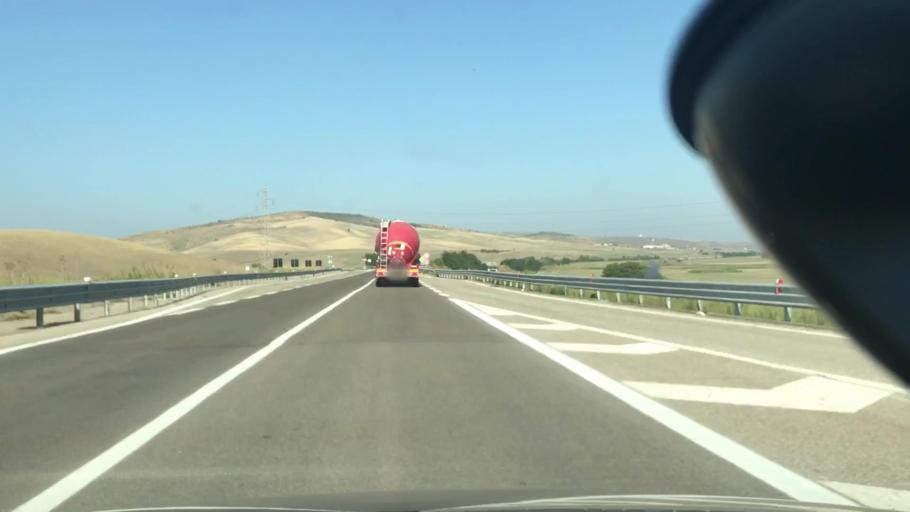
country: IT
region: Basilicate
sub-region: Provincia di Matera
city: Irsina
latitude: 40.7880
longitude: 16.2902
